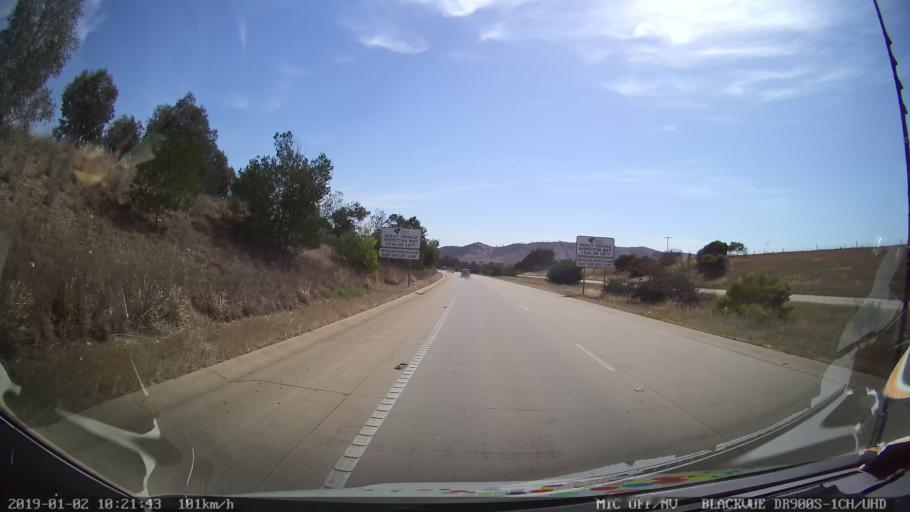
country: AU
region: New South Wales
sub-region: Gundagai
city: Gundagai
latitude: -34.9796
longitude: 148.1389
